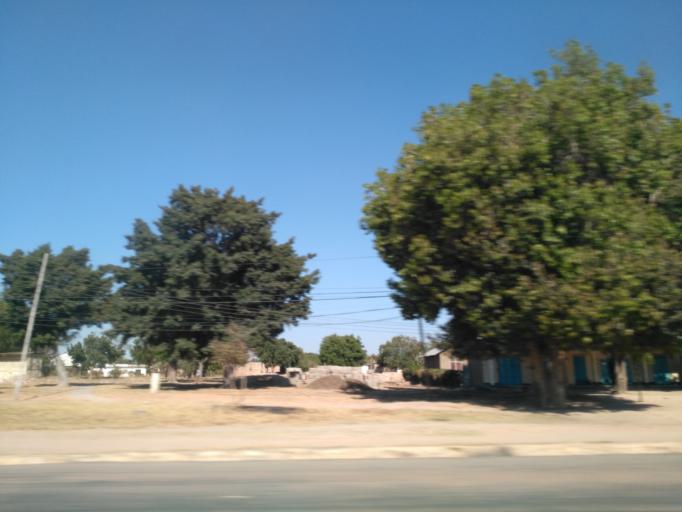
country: TZ
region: Dodoma
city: Dodoma
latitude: -6.1365
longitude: 35.7466
